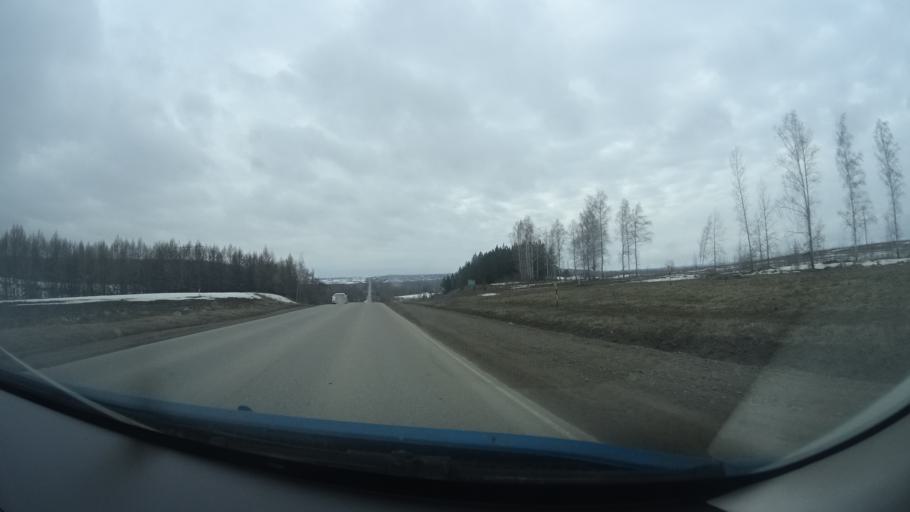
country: RU
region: Bashkortostan
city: Birsk
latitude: 55.4873
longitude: 55.5994
